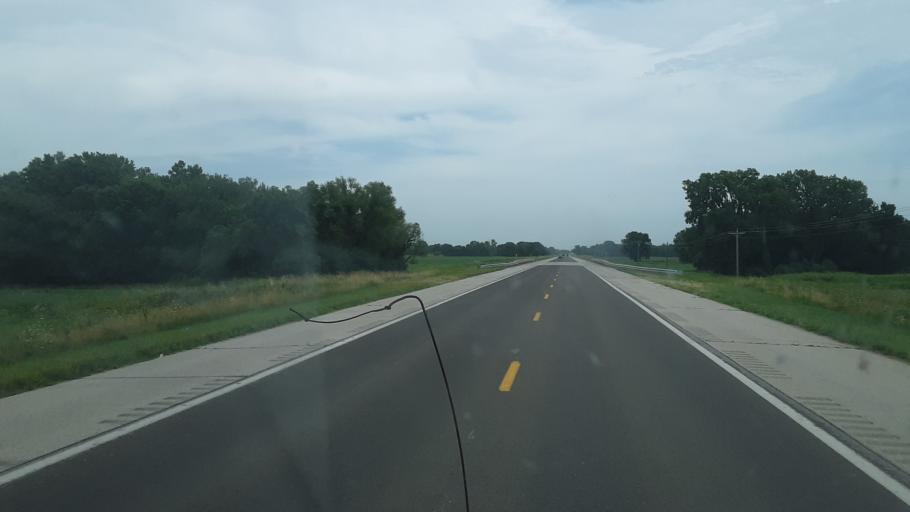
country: US
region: Kansas
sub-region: Allen County
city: Iola
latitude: 37.9219
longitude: -95.4413
